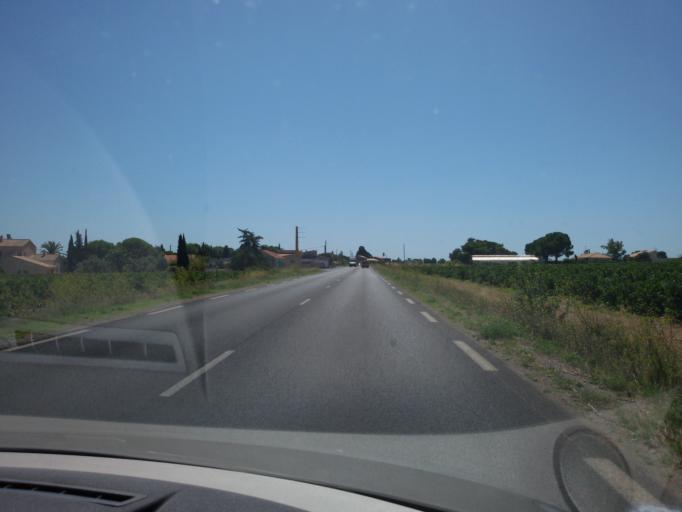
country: FR
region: Languedoc-Roussillon
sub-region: Departement de l'Herault
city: Vic-la-Gardiole
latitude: 43.4862
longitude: 3.7724
